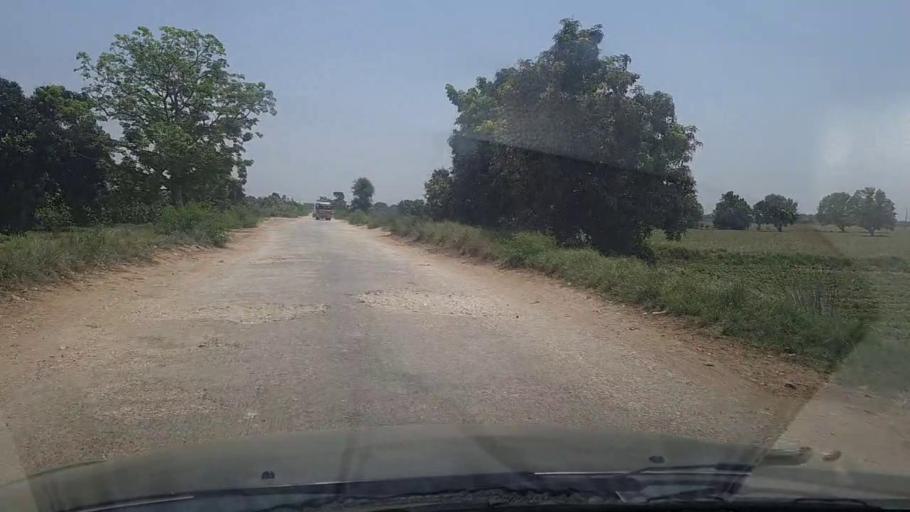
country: PK
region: Sindh
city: Tando Muhammad Khan
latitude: 25.2744
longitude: 68.6249
